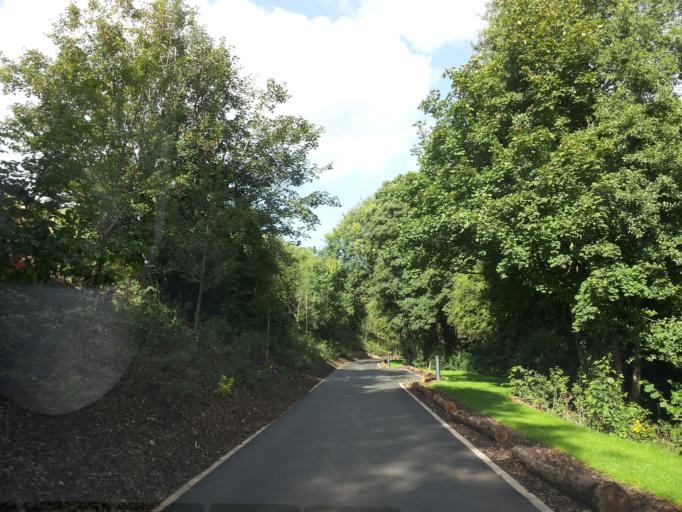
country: GB
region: England
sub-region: Bath and North East Somerset
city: Corston
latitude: 51.3795
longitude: -2.4123
